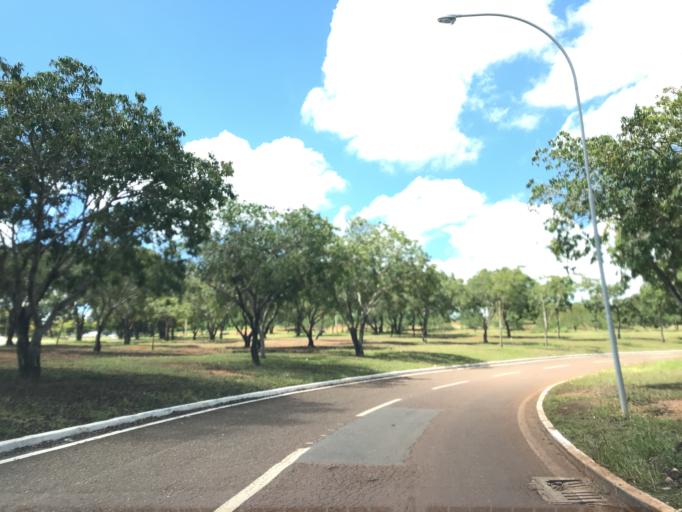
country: BR
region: Federal District
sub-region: Brasilia
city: Brasilia
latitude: -15.7572
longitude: -47.9263
